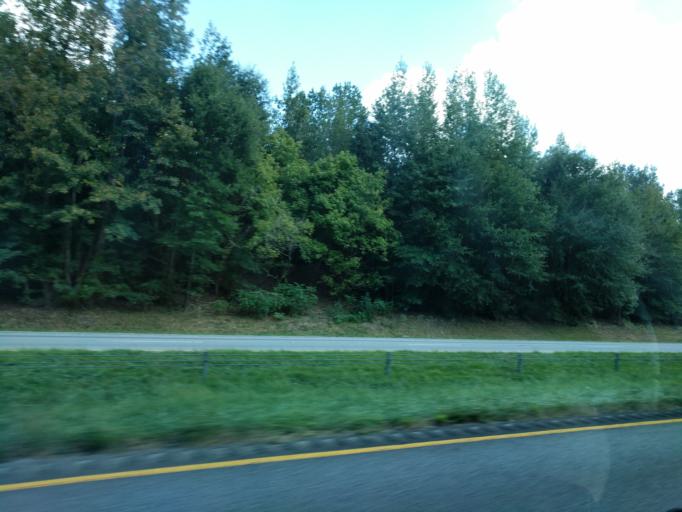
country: US
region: South Carolina
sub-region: Spartanburg County
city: Roebuck
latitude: 34.8693
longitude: -81.9876
